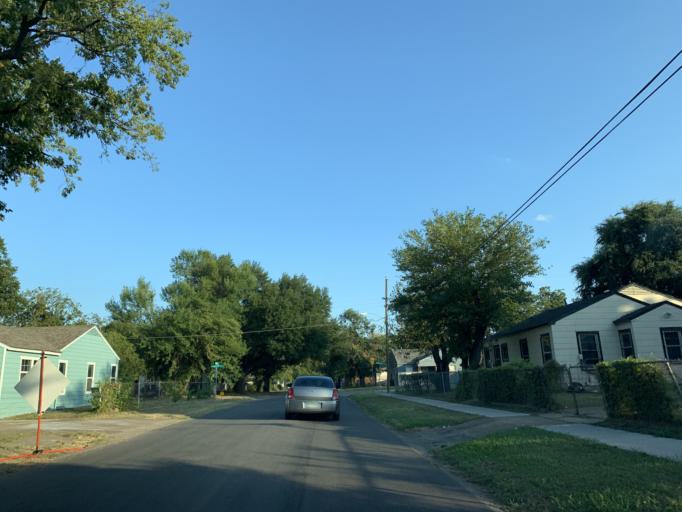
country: US
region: Texas
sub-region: Dallas County
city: Dallas
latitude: 32.7070
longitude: -96.7903
